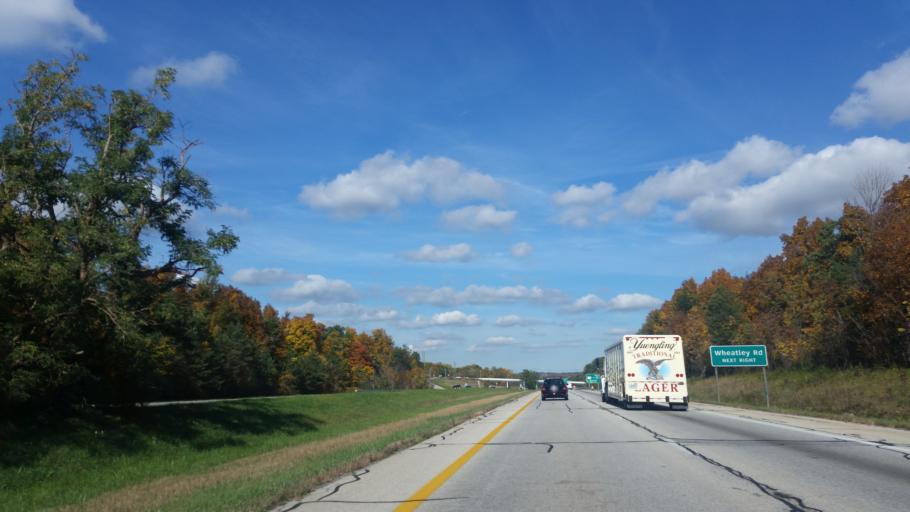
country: US
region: Ohio
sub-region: Summit County
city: Richfield
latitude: 41.2144
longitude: -81.6258
